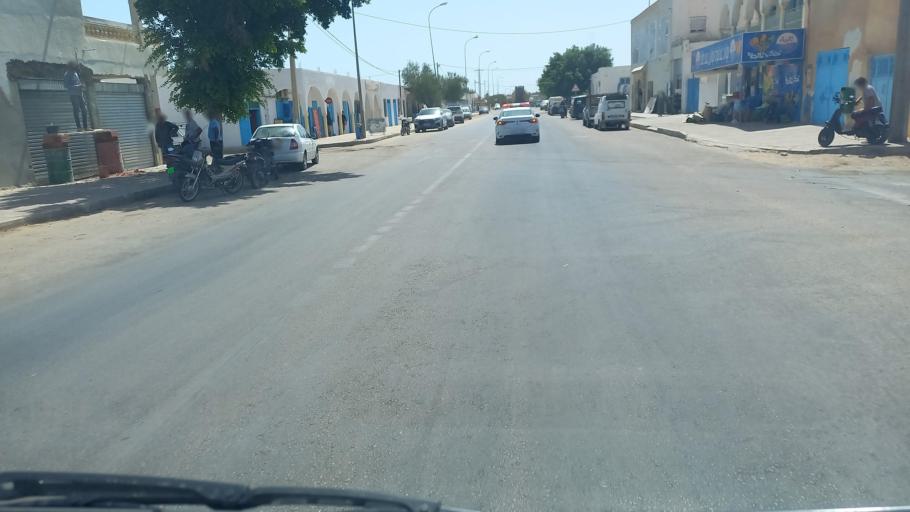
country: TN
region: Madanin
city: Midoun
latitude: 33.7758
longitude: 10.8945
